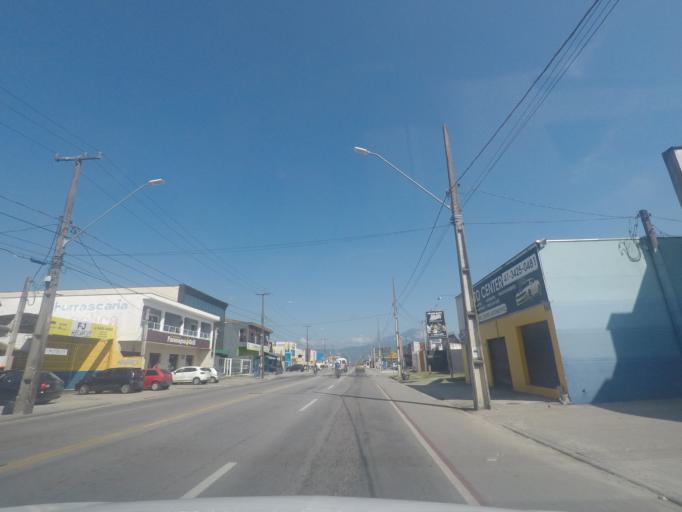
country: BR
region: Parana
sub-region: Paranagua
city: Paranagua
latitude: -25.5551
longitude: -48.5544
